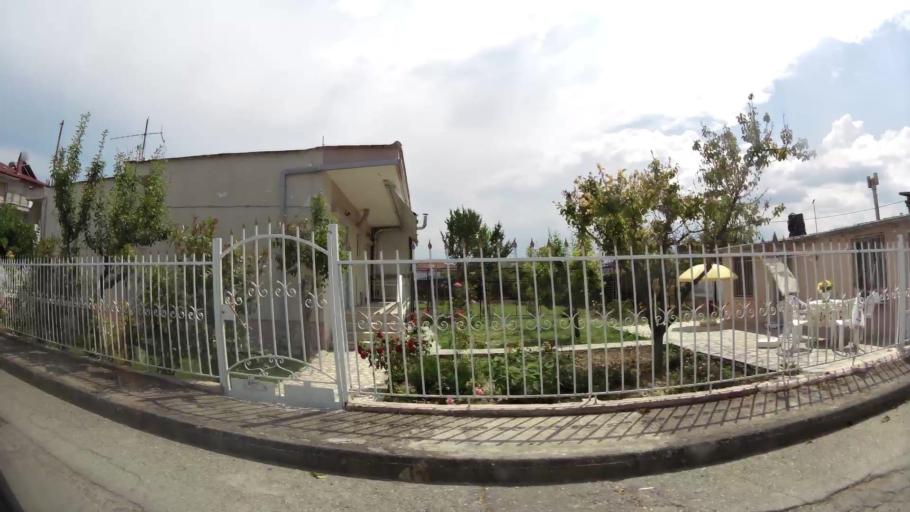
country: GR
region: Central Macedonia
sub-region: Nomos Pierias
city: Korinos
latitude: 40.3211
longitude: 22.5890
